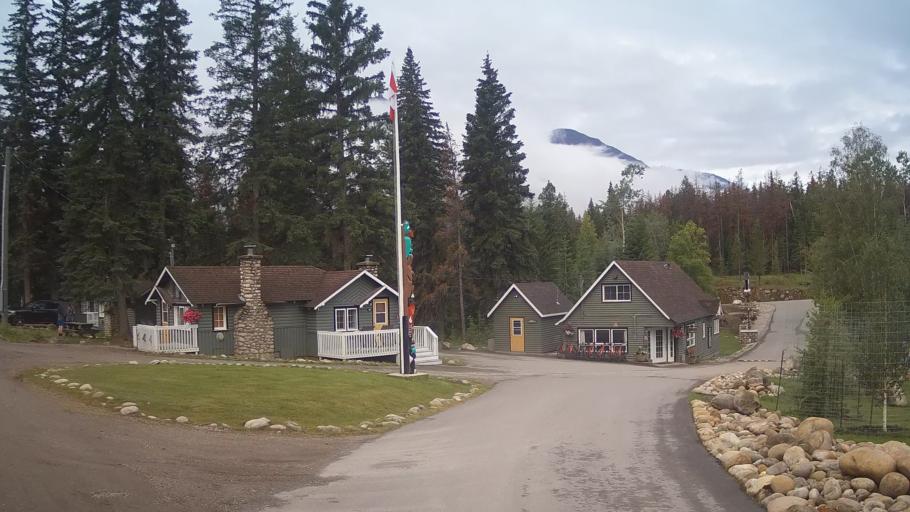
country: CA
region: Alberta
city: Jasper Park Lodge
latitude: 52.8680
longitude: -118.0709
